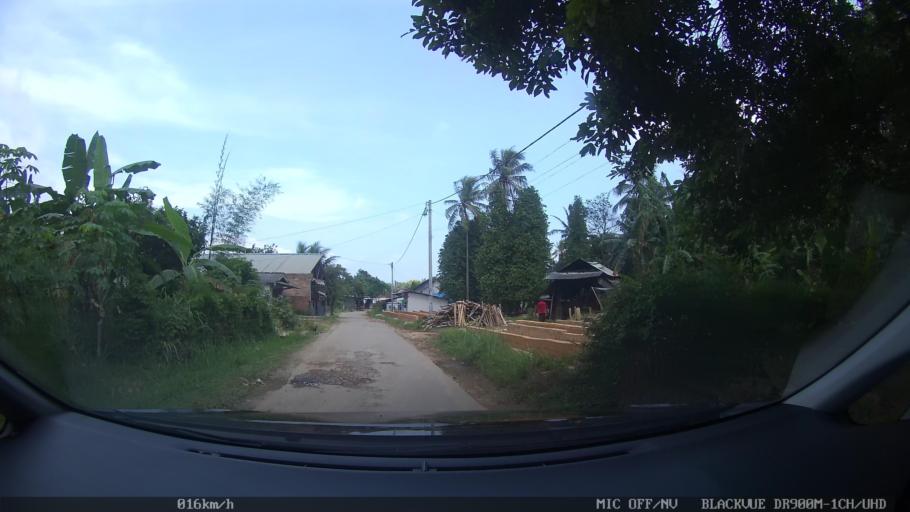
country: ID
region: Lampung
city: Kedaton
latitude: -5.3314
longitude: 105.2888
